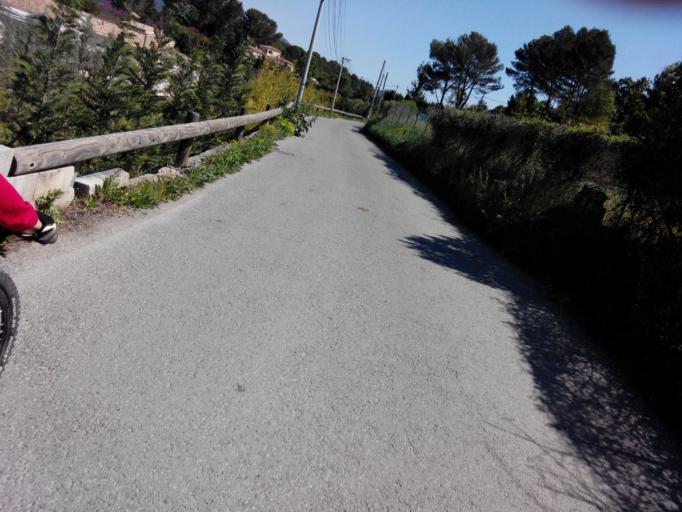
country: FR
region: Provence-Alpes-Cote d'Azur
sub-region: Departement des Bouches-du-Rhone
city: Auriol
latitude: 43.3565
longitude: 5.6326
